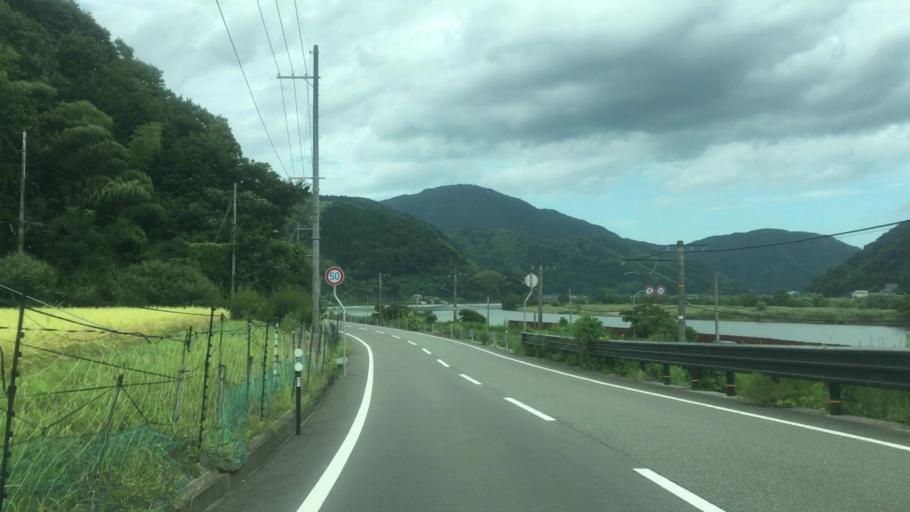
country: JP
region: Hyogo
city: Toyooka
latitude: 35.5748
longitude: 134.8047
